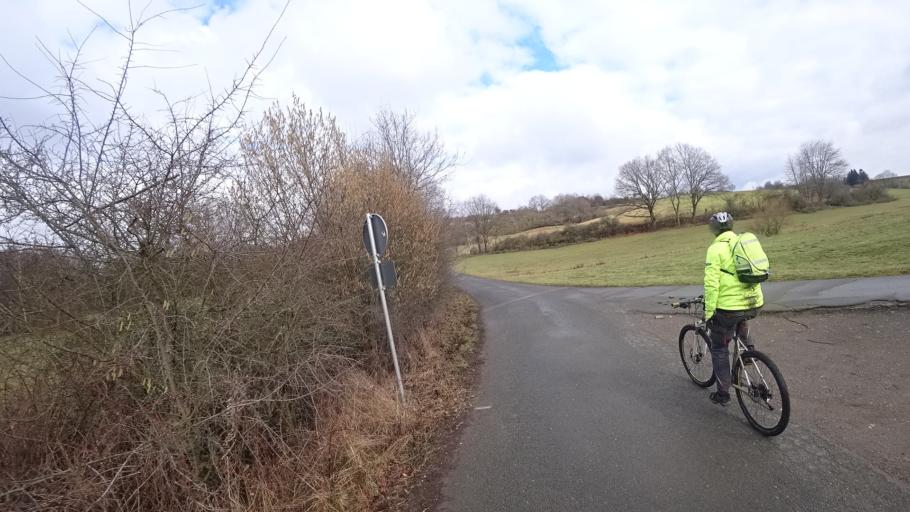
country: DE
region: Rheinland-Pfalz
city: Buch
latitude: 50.1875
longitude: 7.8684
